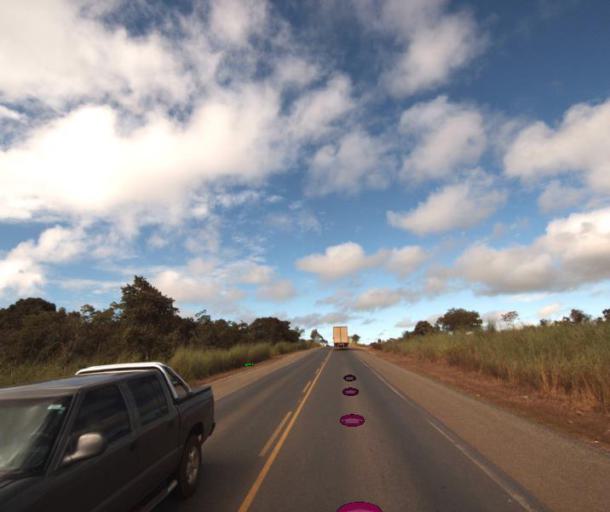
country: BR
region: Goias
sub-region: Uruacu
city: Uruacu
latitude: -14.7789
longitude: -49.2713
